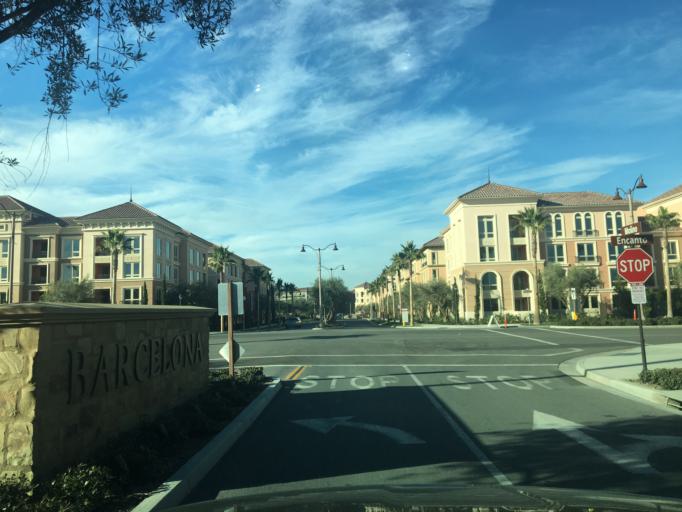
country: US
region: California
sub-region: Orange County
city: Laguna Woods
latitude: 33.6396
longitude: -117.7439
